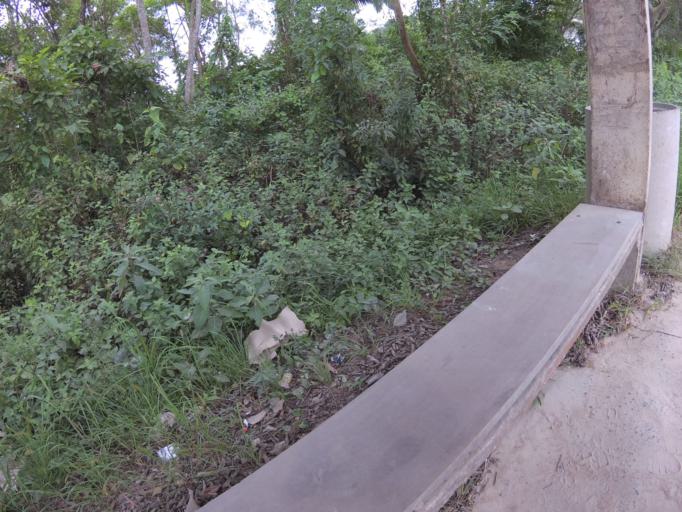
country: BR
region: Santa Catarina
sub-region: Pomerode
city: Pomerode
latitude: -26.8313
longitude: -49.1625
